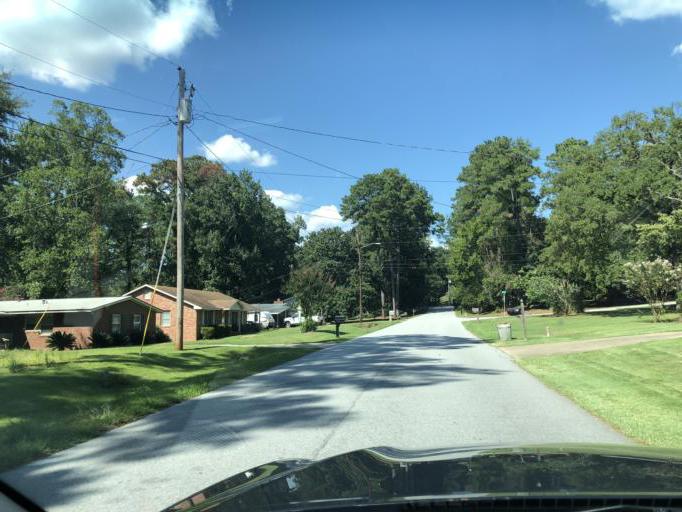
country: US
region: Georgia
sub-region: Muscogee County
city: Columbus
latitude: 32.5378
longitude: -84.9271
